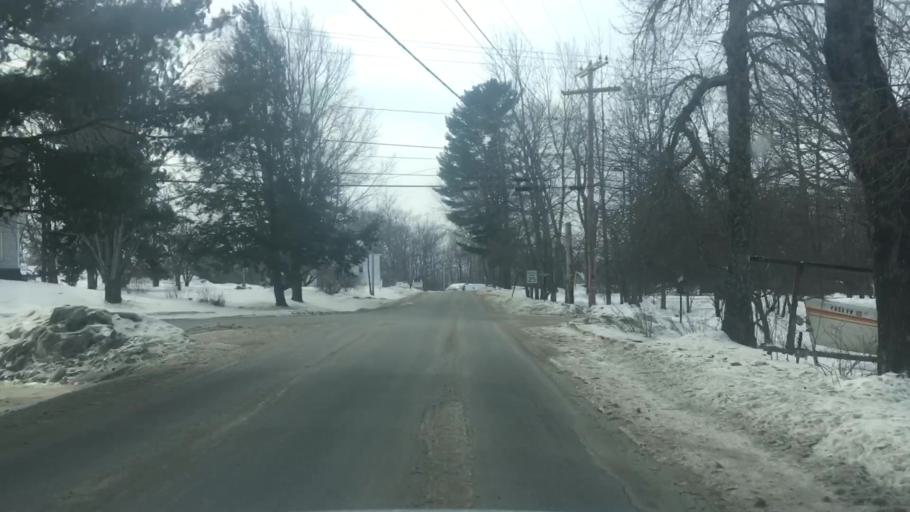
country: US
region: Maine
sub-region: Hancock County
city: Orland
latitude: 44.5708
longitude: -68.7355
